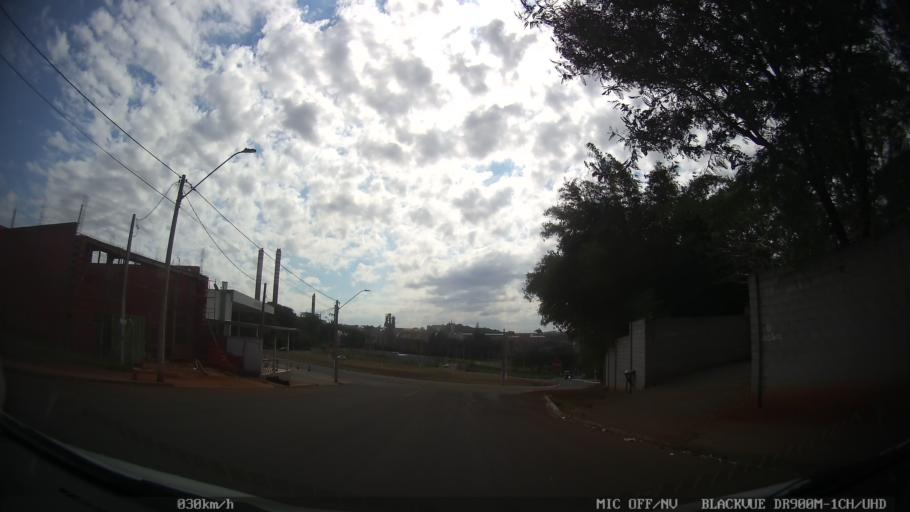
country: BR
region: Sao Paulo
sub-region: Americana
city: Americana
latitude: -22.7153
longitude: -47.3242
